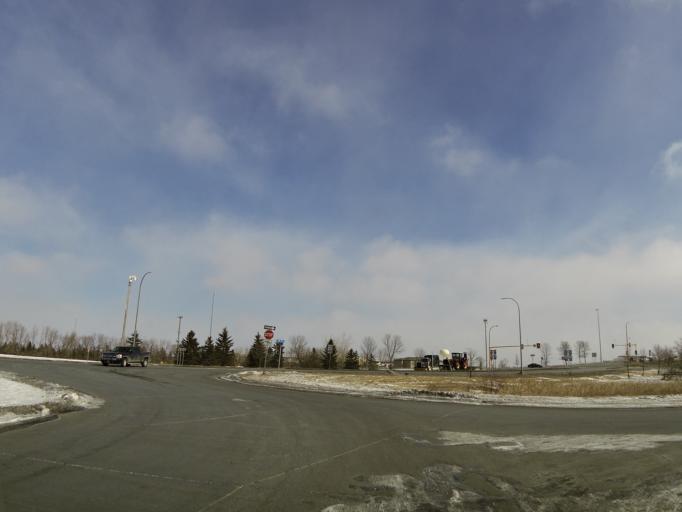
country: US
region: North Dakota
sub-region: Grand Forks County
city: Grand Forks
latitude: 47.8890
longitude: -97.0921
